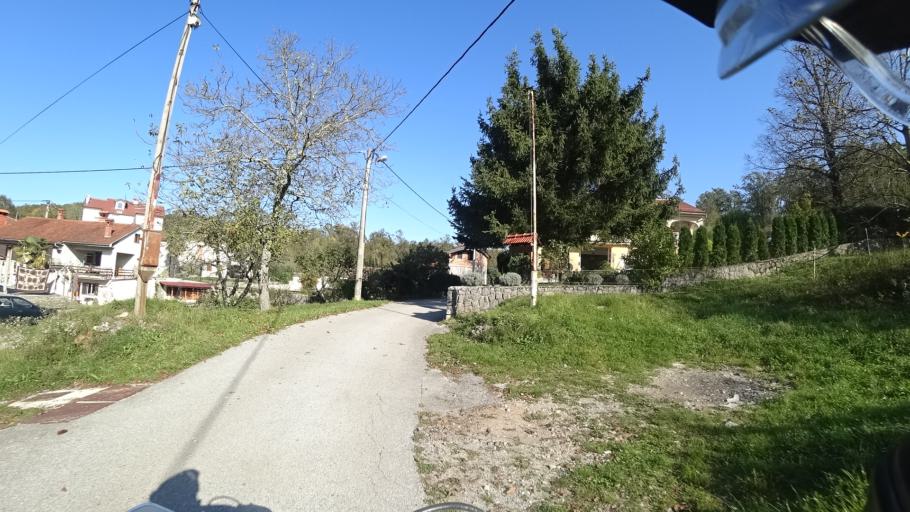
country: HR
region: Primorsko-Goranska
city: Kastav
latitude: 45.3933
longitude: 14.3251
